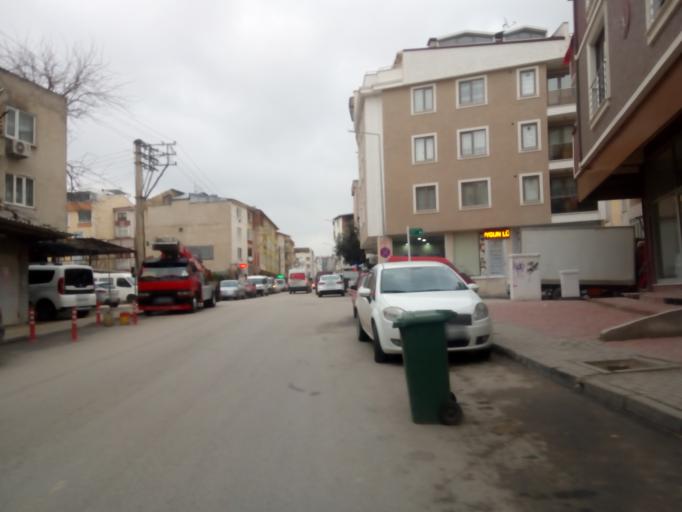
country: TR
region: Bursa
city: Niluefer
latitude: 40.2538
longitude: 28.9606
